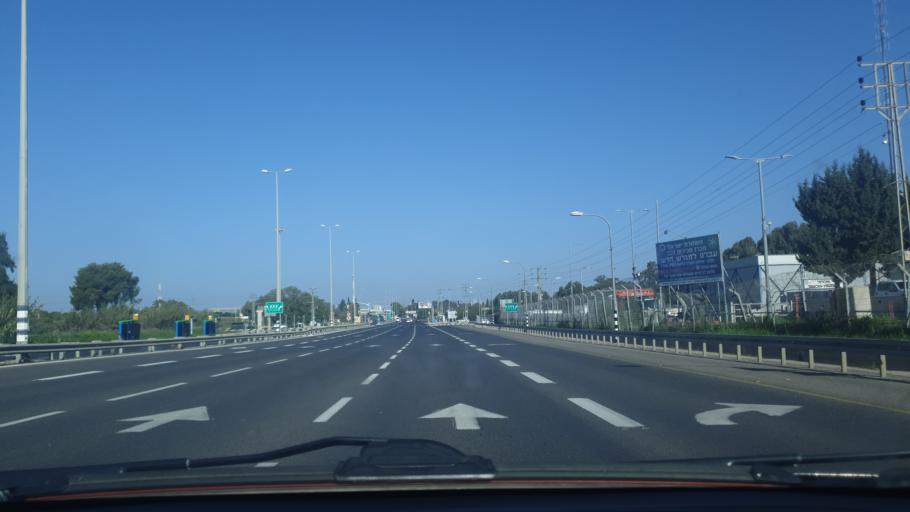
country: IL
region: Central District
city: Bet Dagan
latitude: 31.9996
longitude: 34.8224
